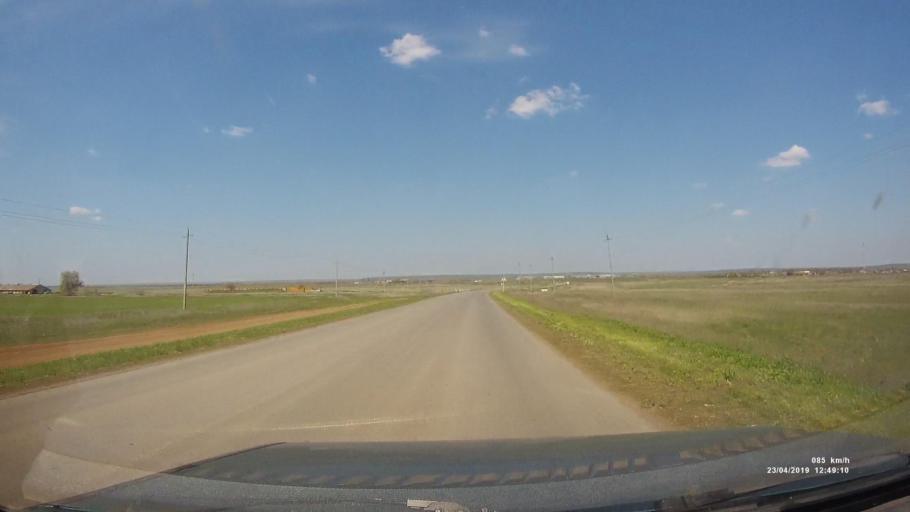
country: RU
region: Kalmykiya
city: Yashalta
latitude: 46.5339
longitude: 42.6388
